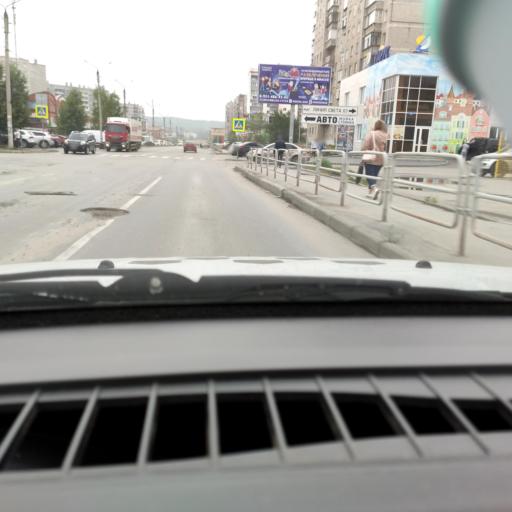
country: RU
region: Chelyabinsk
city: Miass
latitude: 55.0455
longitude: 60.1031
